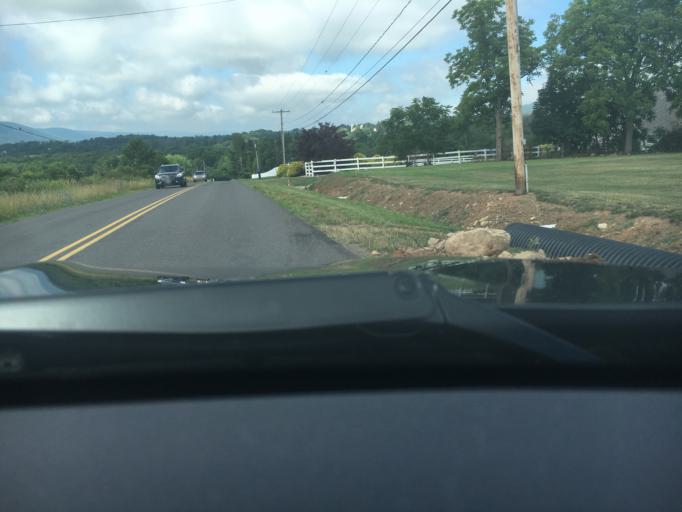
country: US
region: Pennsylvania
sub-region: Luzerne County
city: Conyngham
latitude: 41.0278
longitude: -76.0495
